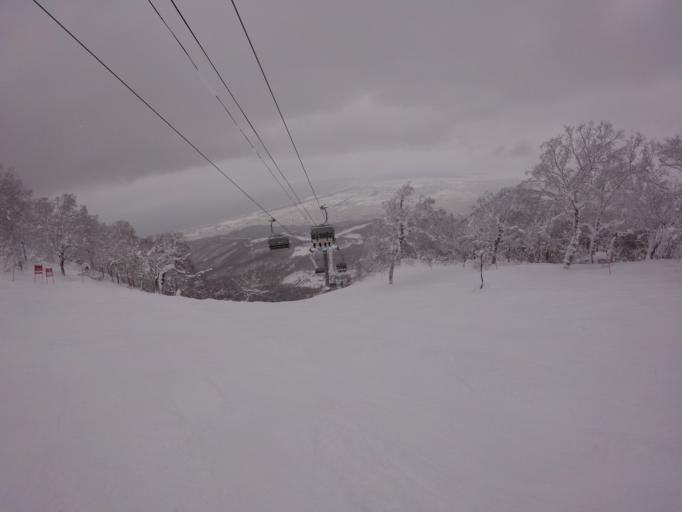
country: JP
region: Hokkaido
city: Sapporo
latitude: 43.0768
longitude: 141.1980
